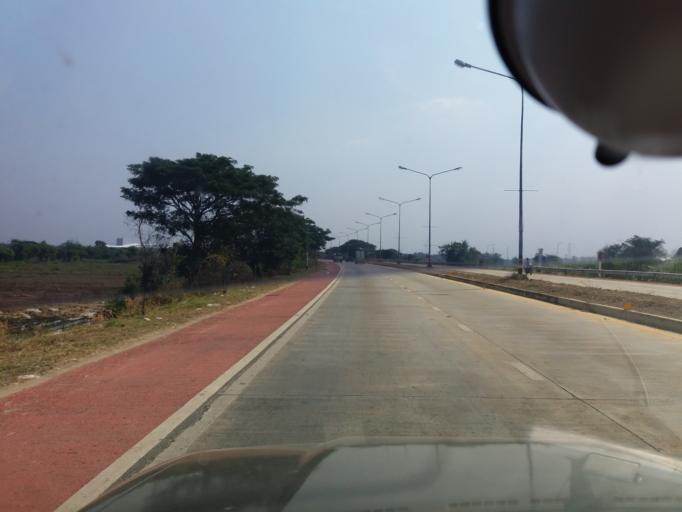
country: TH
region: Sing Buri
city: Sing Buri
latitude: 14.8799
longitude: 100.3928
